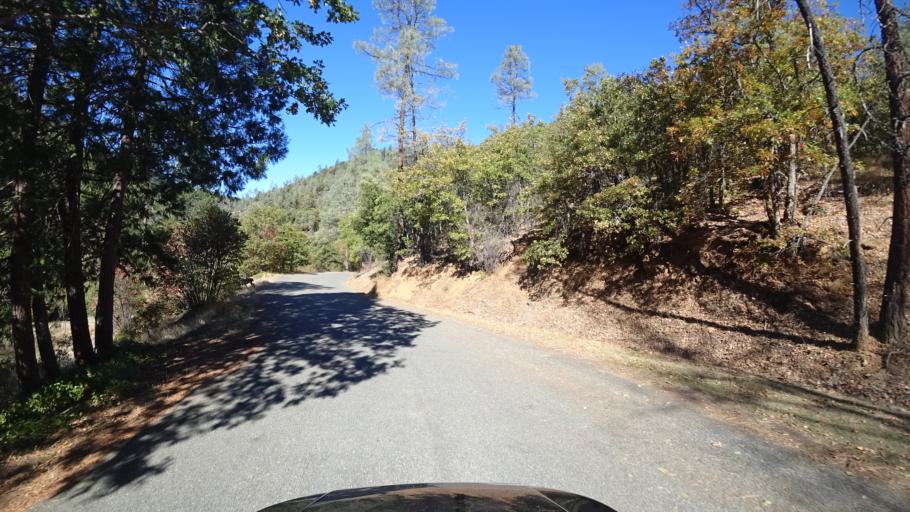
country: US
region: California
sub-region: Humboldt County
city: Willow Creek
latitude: 41.2181
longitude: -123.2370
